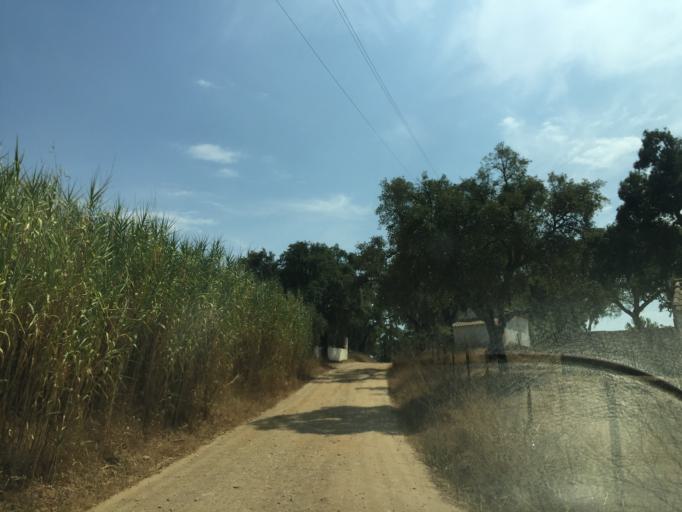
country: PT
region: Setubal
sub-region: Grandola
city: Grandola
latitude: 38.0114
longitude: -8.4843
